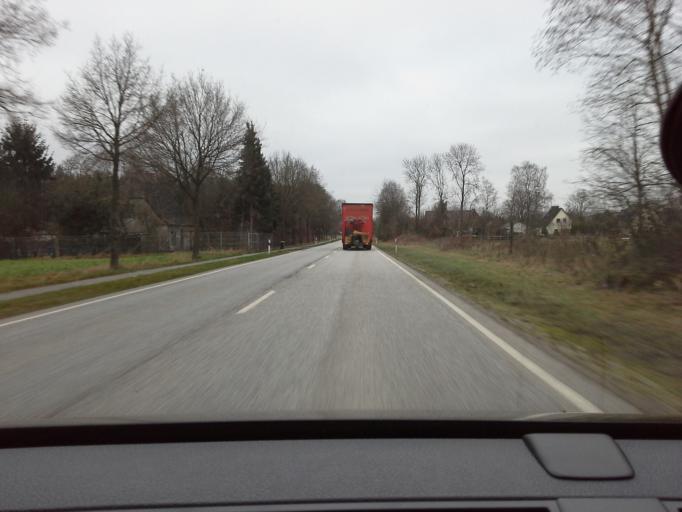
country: DE
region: Schleswig-Holstein
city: Lentfohrden
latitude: 53.8626
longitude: 9.8886
